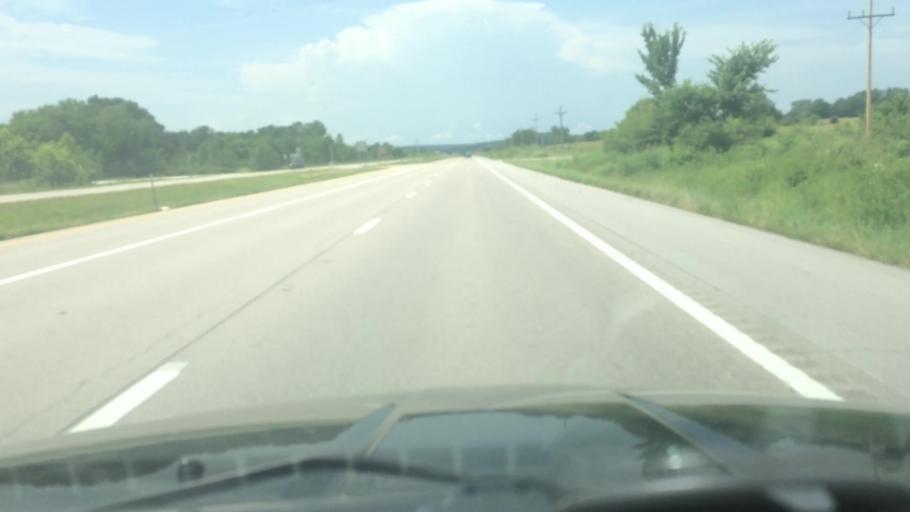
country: US
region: Missouri
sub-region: Polk County
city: Humansville
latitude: 37.8045
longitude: -93.5986
